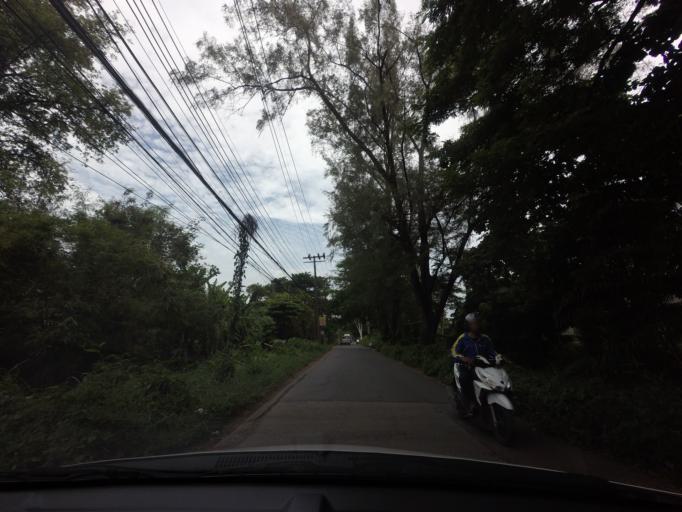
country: TH
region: Bangkok
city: Lak Si
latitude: 13.8558
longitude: 100.5802
